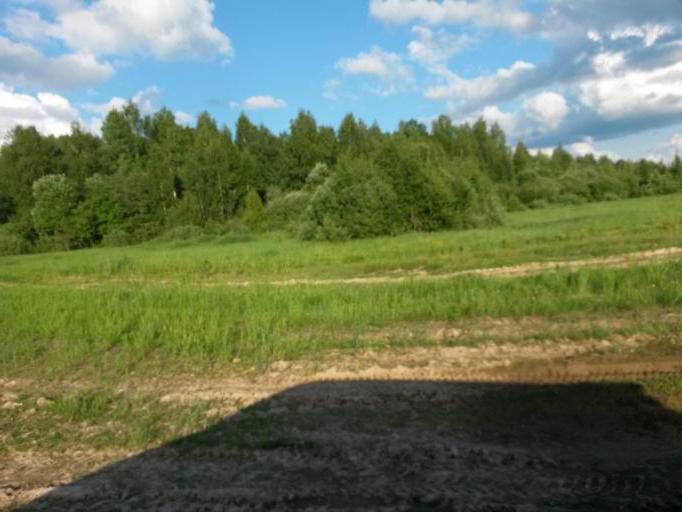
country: RU
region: Jaroslavl
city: Burmakino
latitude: 57.3670
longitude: 40.2005
